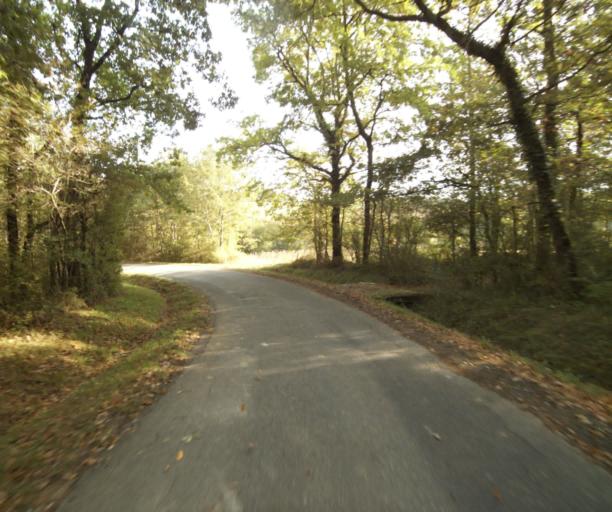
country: FR
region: Midi-Pyrenees
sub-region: Departement de la Haute-Garonne
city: Villemur-sur-Tarn
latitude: 43.9094
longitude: 1.5036
